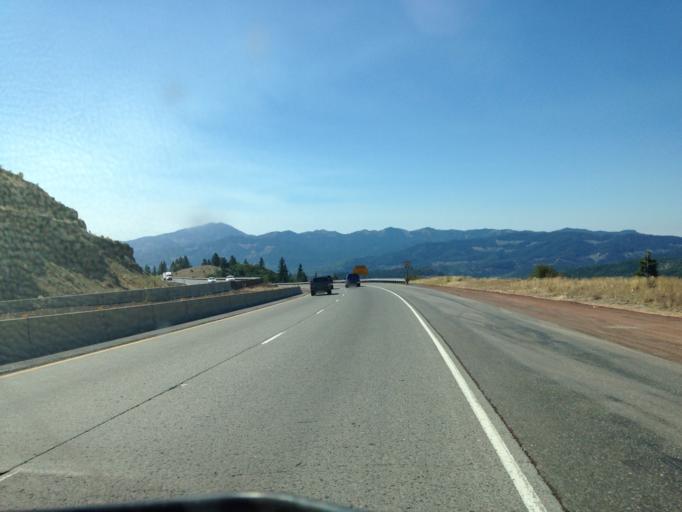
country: US
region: Oregon
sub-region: Jackson County
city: Ashland
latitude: 42.0573
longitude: -122.6095
